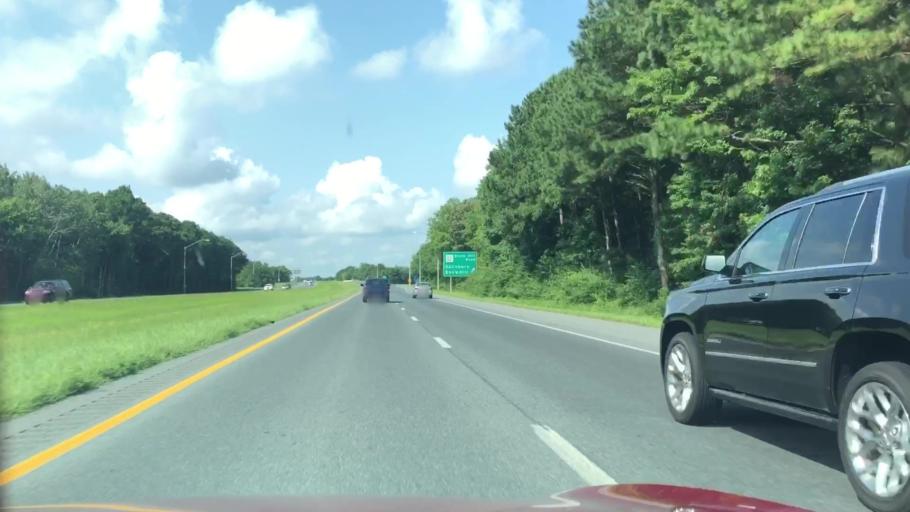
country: US
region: Maryland
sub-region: Wicomico County
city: Salisbury
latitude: 38.3364
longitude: -75.5624
